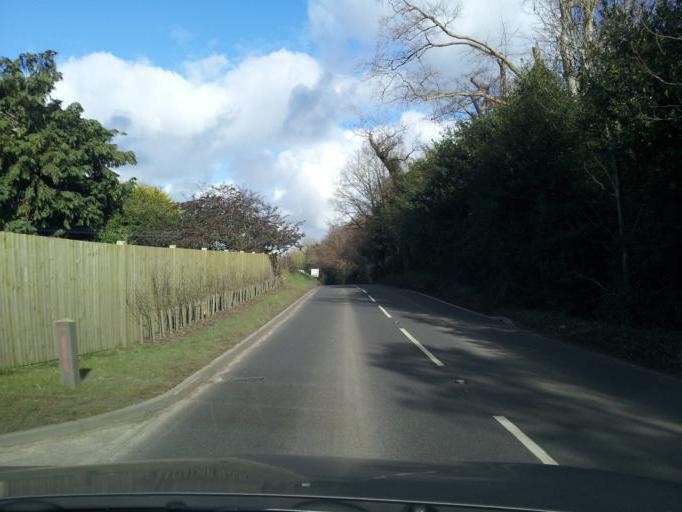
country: GB
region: England
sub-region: Norfolk
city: Mattishall
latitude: 52.6797
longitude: 1.1066
